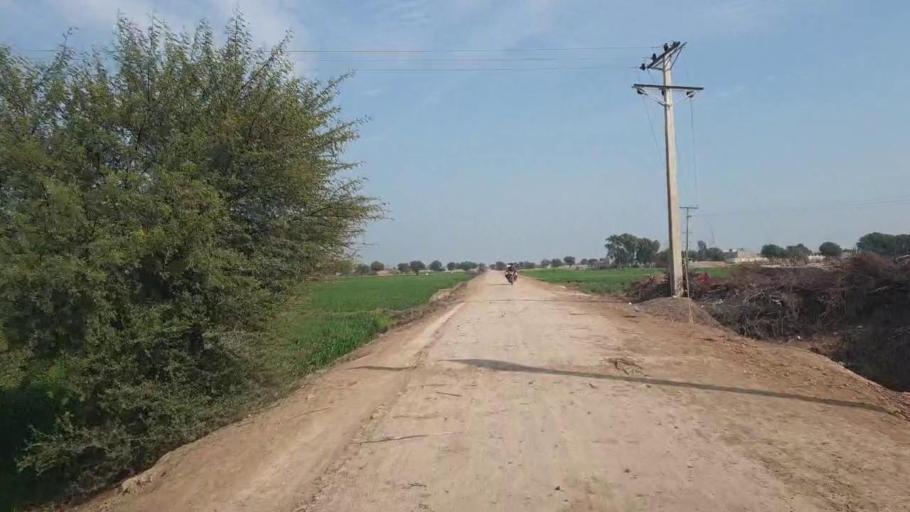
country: PK
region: Sindh
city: Shahdadpur
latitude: 26.0151
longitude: 68.5479
